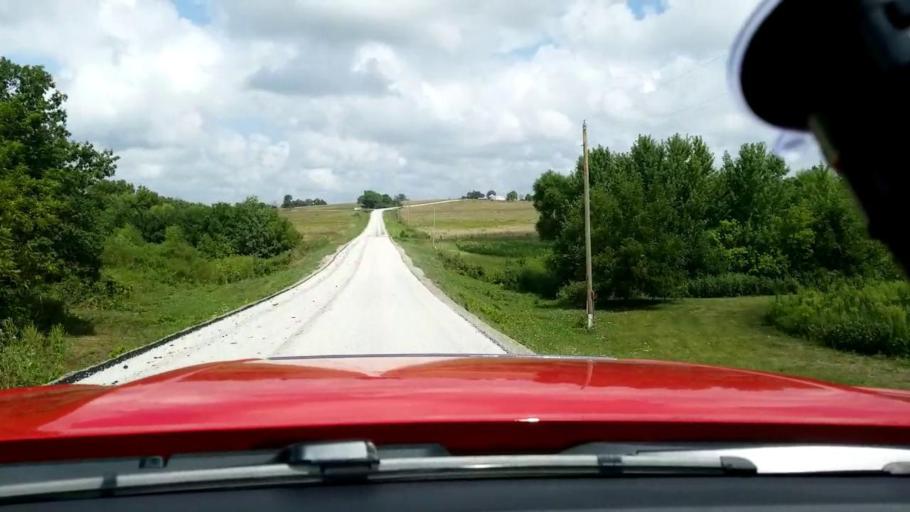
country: US
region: Iowa
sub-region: Decatur County
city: Lamoni
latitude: 40.6478
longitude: -94.0529
